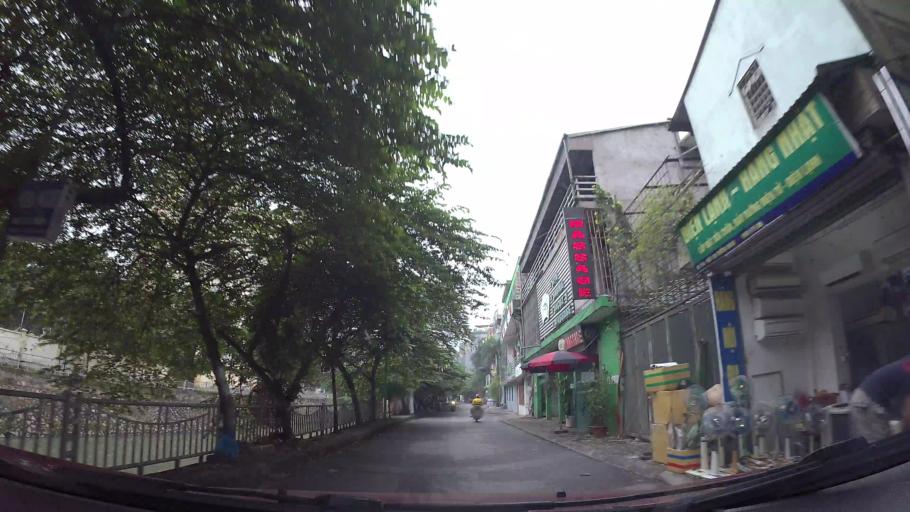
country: VN
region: Ha Noi
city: Hai BaTrung
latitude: 20.9998
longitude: 105.8356
